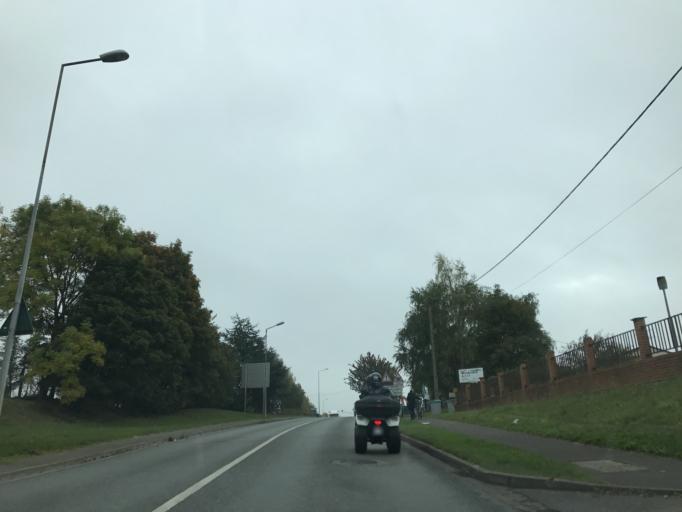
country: FR
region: Nord-Pas-de-Calais
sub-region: Departement du Pas-de-Calais
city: Saint-Laurent-Blangy
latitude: 50.2948
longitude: 2.8047
